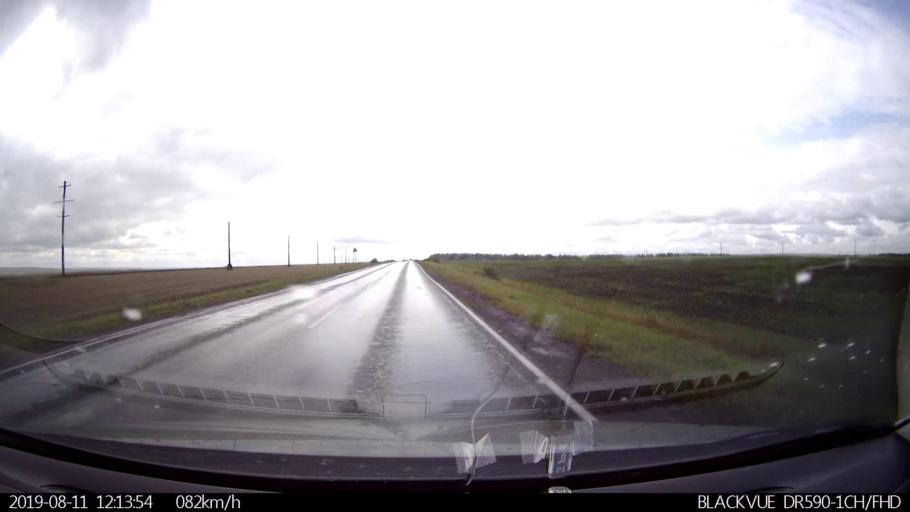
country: RU
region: Ulyanovsk
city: Ignatovka
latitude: 53.9573
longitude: 47.9870
